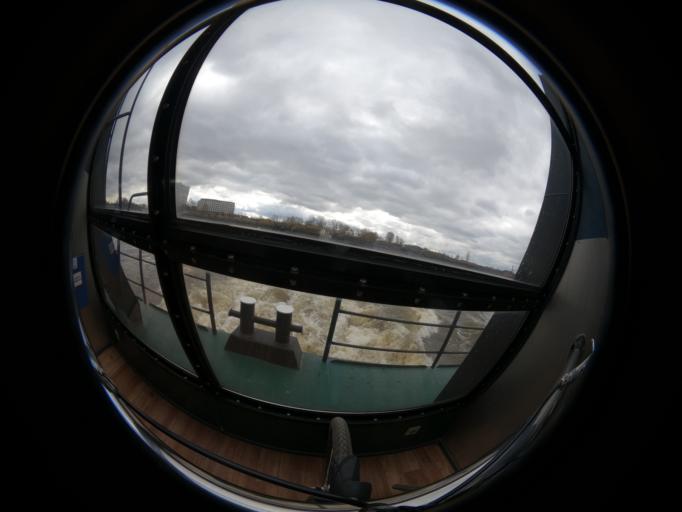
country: DE
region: Hamburg
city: Altona
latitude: 53.5438
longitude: 9.8612
